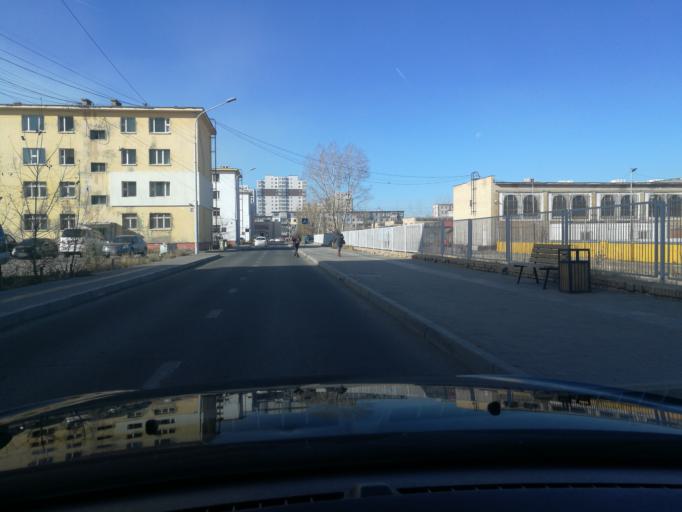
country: MN
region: Ulaanbaatar
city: Ulaanbaatar
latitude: 47.9011
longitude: 106.9062
